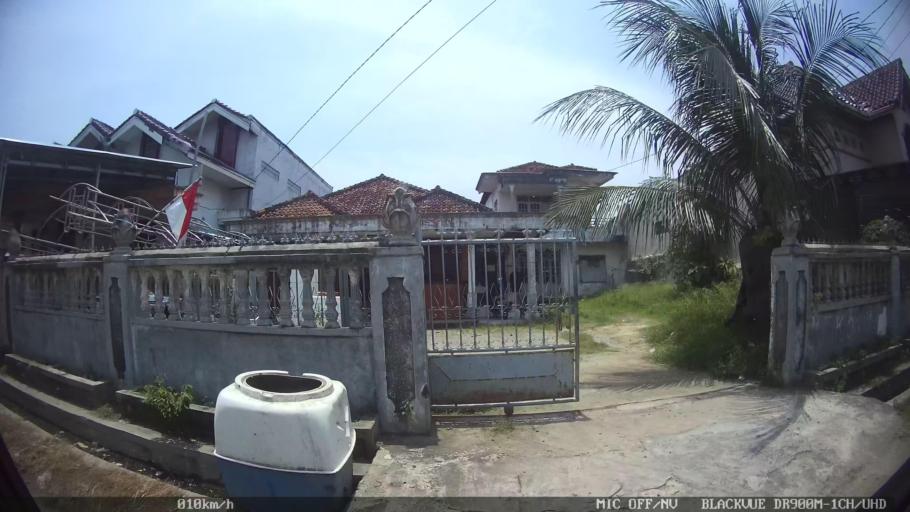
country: ID
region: Lampung
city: Bandarlampung
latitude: -5.4588
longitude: 105.2590
